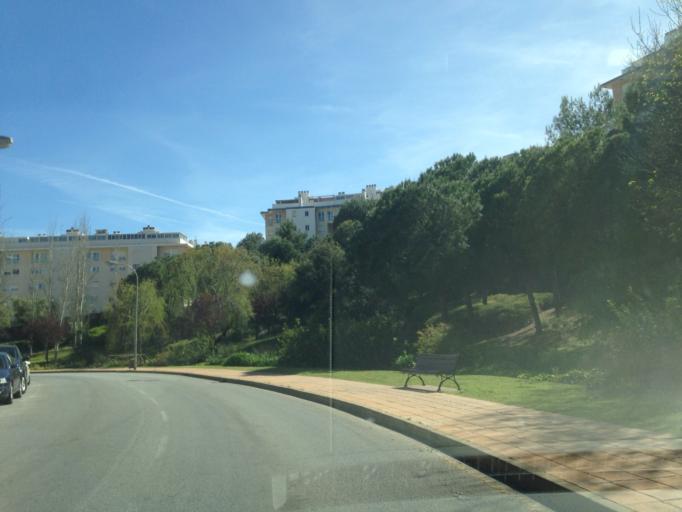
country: ES
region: Andalusia
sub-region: Provincia de Malaga
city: Benalmadena
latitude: 36.5977
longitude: -4.5422
